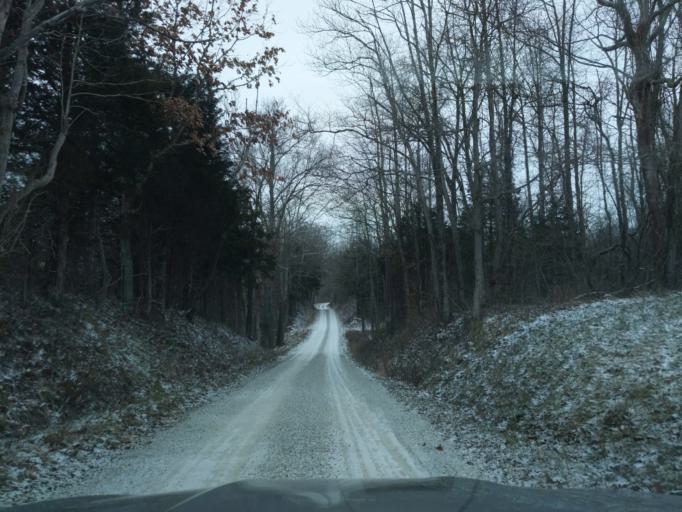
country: US
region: Indiana
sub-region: Decatur County
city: Westport
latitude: 39.2082
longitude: -85.4445
